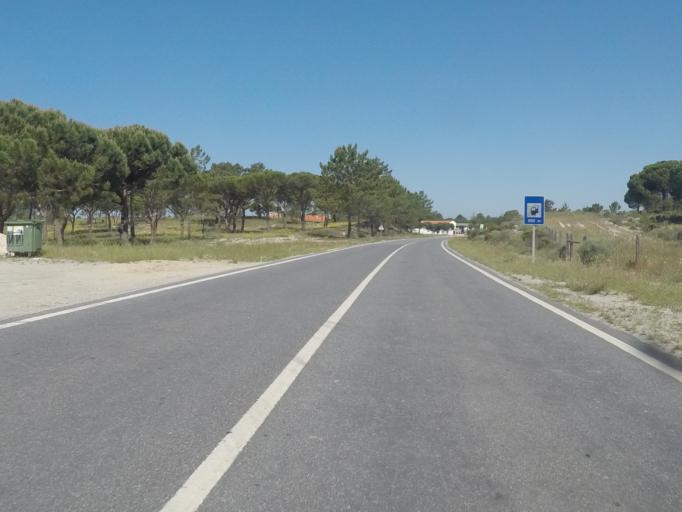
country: PT
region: Setubal
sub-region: Grandola
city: Grandola
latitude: 38.3076
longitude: -8.7406
